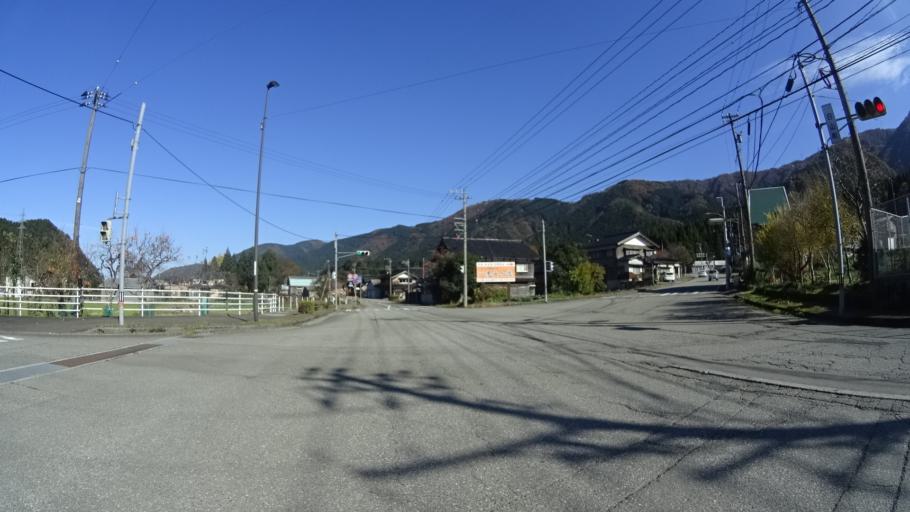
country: JP
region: Ishikawa
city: Tsurugi-asahimachi
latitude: 36.4280
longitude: 136.6333
